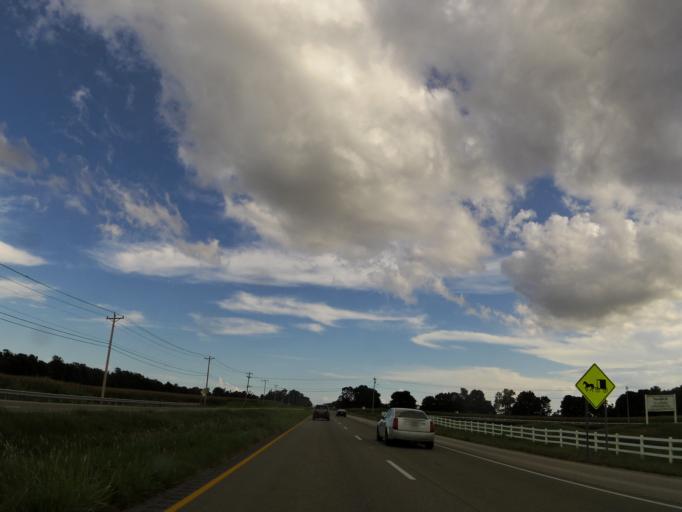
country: US
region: Kentucky
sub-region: Christian County
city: Oak Grove
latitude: 36.7526
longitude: -87.4694
